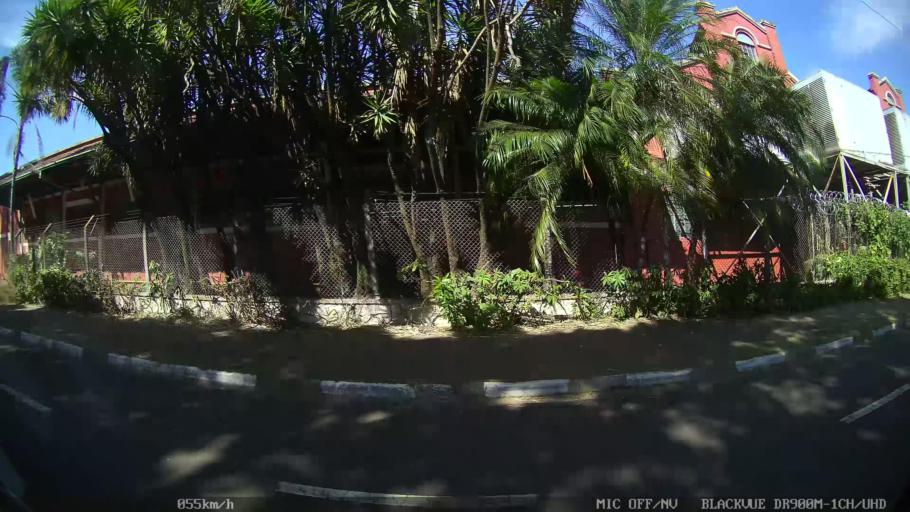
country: BR
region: Sao Paulo
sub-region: Franca
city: Franca
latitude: -20.5379
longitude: -47.4144
